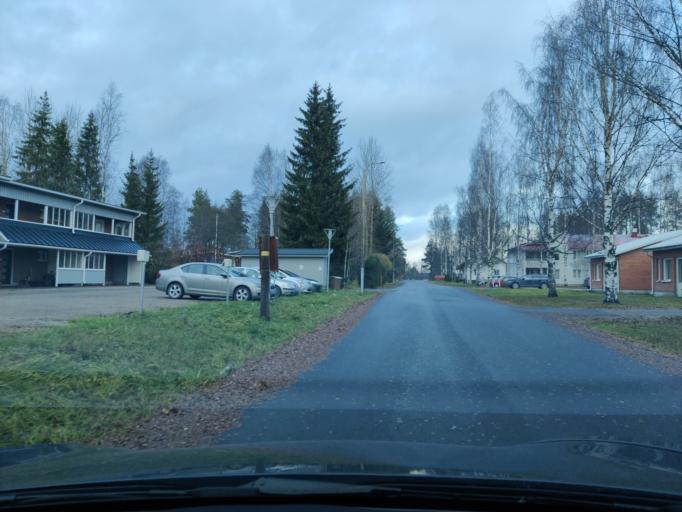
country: FI
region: Northern Savo
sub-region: Ylae-Savo
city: Kiuruvesi
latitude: 63.6465
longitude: 26.6337
